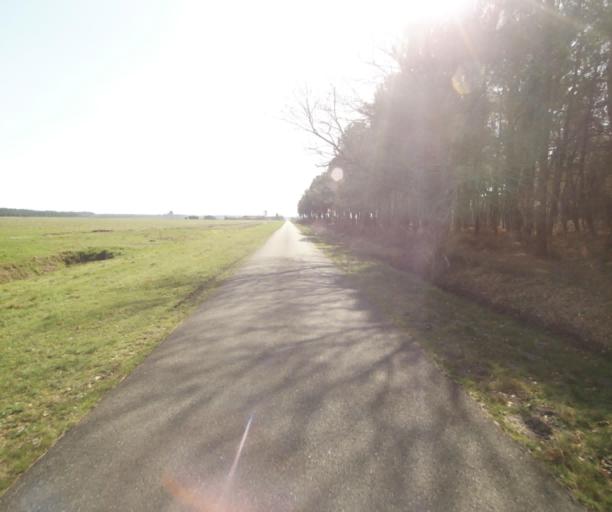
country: FR
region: Aquitaine
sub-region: Departement des Landes
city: Roquefort
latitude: 44.1653
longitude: -0.2515
